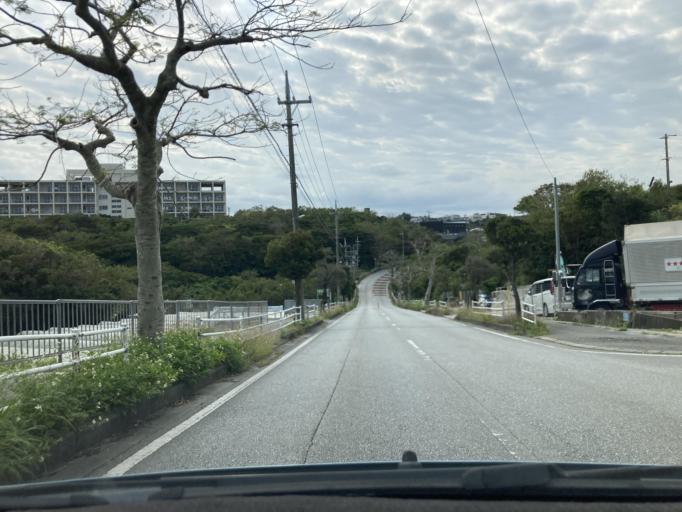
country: JP
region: Okinawa
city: Tomigusuku
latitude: 26.1852
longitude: 127.6952
